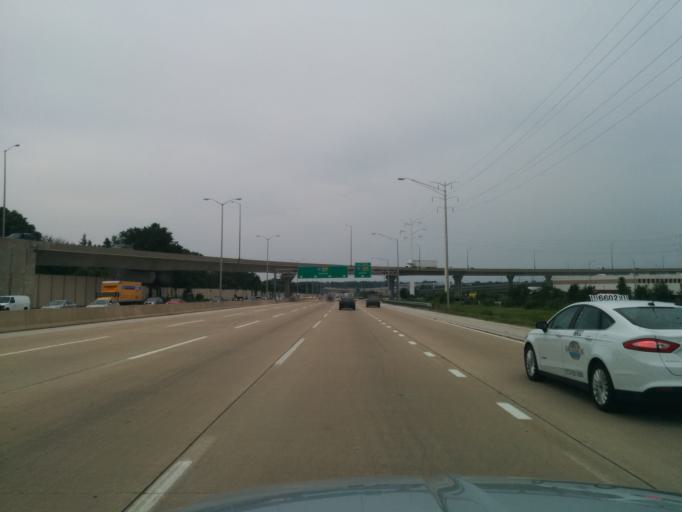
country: US
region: Illinois
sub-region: DuPage County
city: Downers Grove
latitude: 41.8245
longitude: -88.0233
